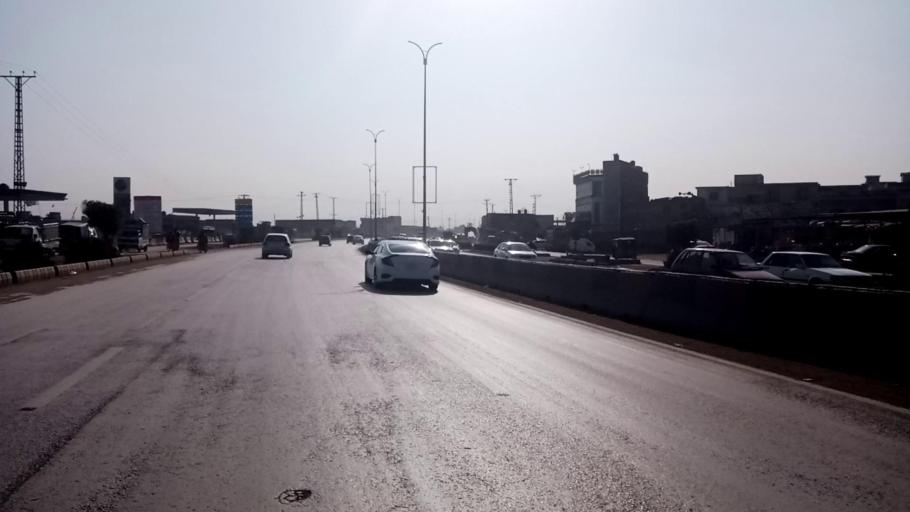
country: PK
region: Khyber Pakhtunkhwa
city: Peshawar
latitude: 34.0119
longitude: 71.6219
